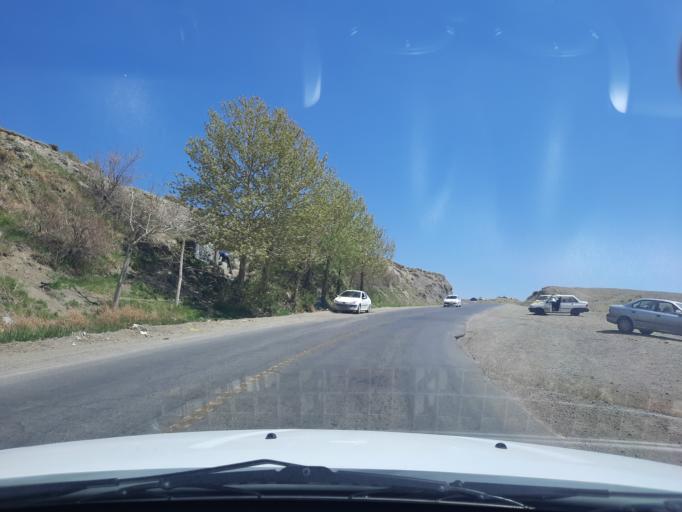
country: IR
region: Qazvin
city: Qazvin
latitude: 36.3567
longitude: 50.1879
